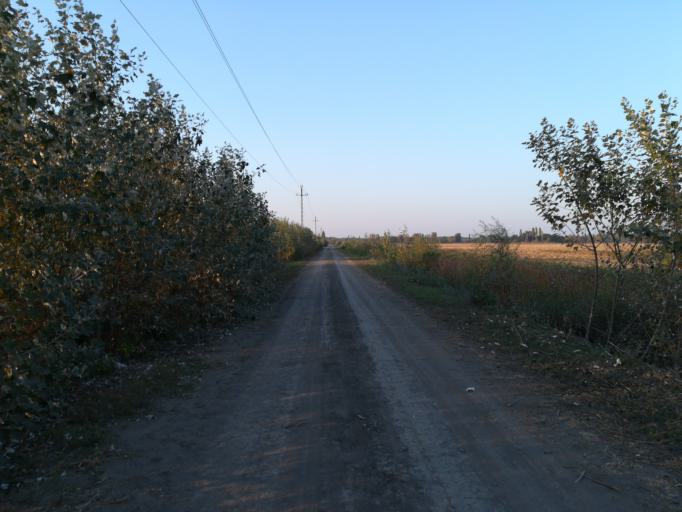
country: HU
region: Bacs-Kiskun
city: Tiszakecske
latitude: 46.9143
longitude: 20.1178
